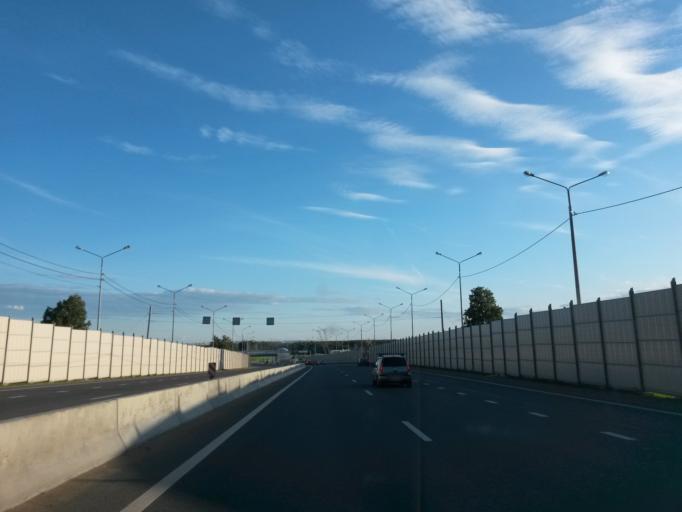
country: RU
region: Jaroslavl
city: Yaroslavl
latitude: 57.7062
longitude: 39.9013
